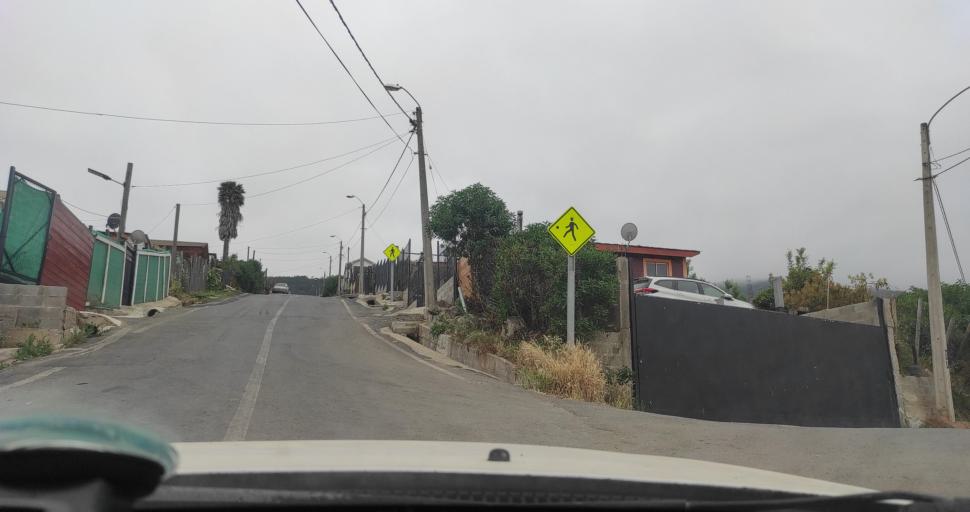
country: CL
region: Valparaiso
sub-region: Provincia de Marga Marga
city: Limache
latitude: -32.9856
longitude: -71.2268
